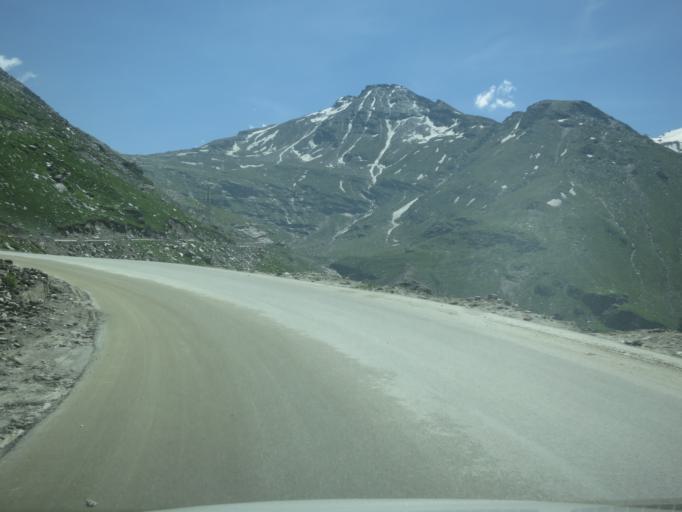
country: IN
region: Himachal Pradesh
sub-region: Kulu
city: Manali
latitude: 32.3536
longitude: 77.2185
